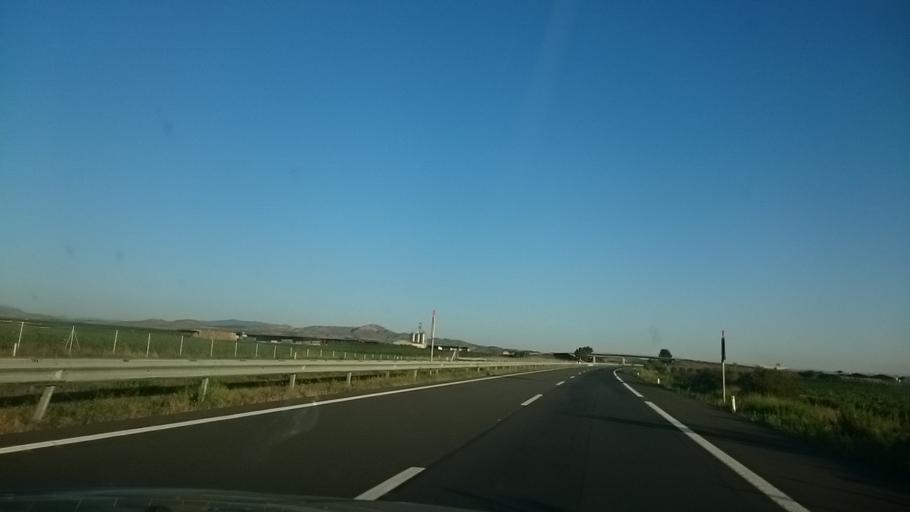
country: ES
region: La Rioja
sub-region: Provincia de La Rioja
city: Aldeanueva de Ebro
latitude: 42.2155
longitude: -1.8873
